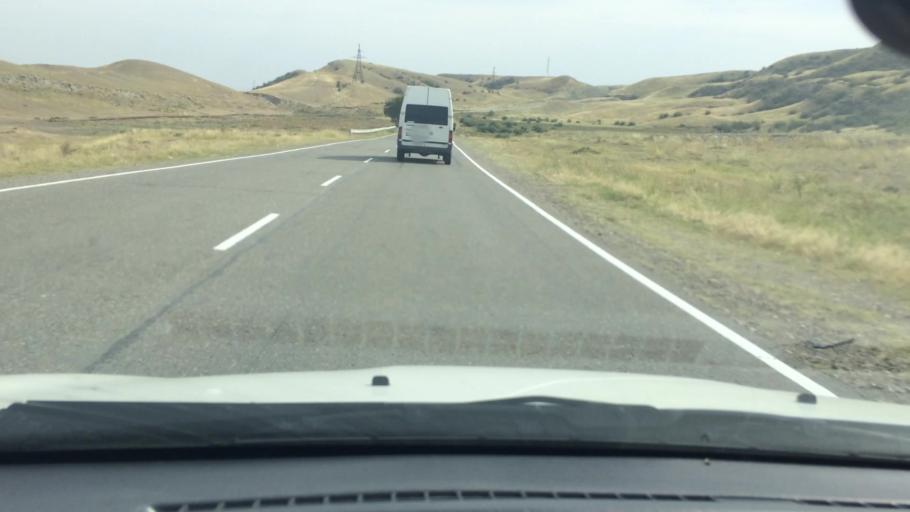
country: GE
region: Kvemo Kartli
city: Rust'avi
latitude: 41.5312
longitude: 44.9844
